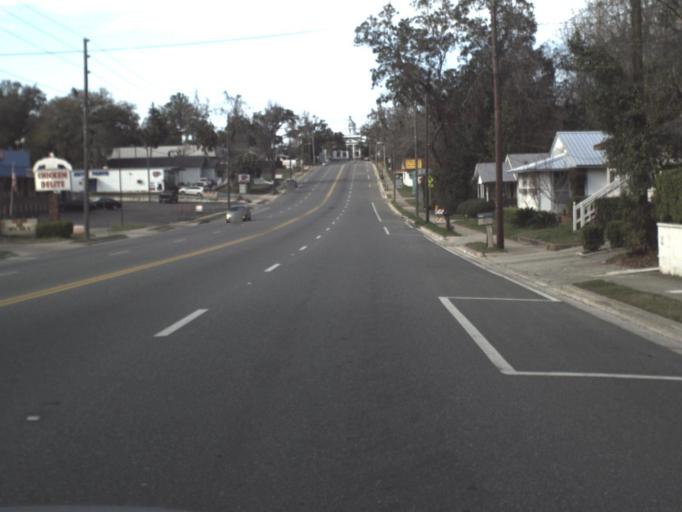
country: US
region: Florida
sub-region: Jefferson County
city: Monticello
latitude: 30.5404
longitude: -83.8701
